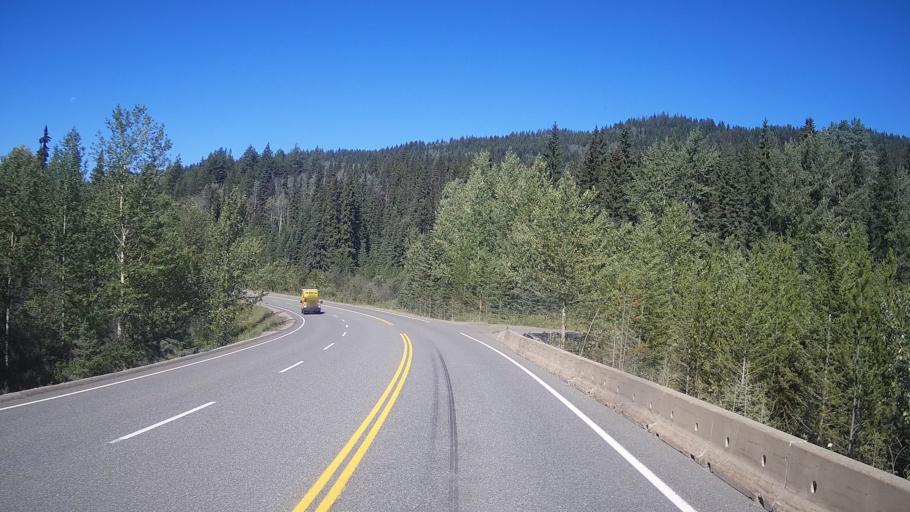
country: CA
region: British Columbia
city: Kamloops
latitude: 51.4776
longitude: -120.4849
